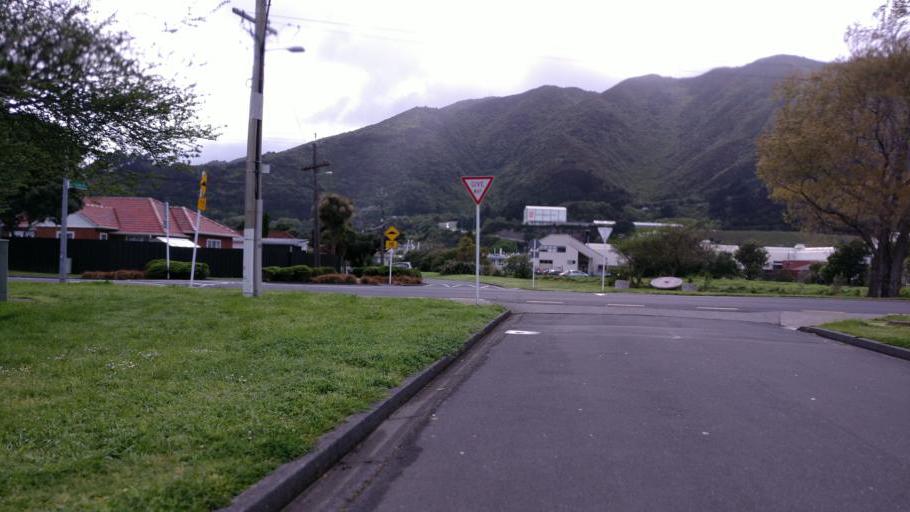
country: NZ
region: Wellington
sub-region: Lower Hutt City
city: Lower Hutt
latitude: -41.2334
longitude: 174.9141
